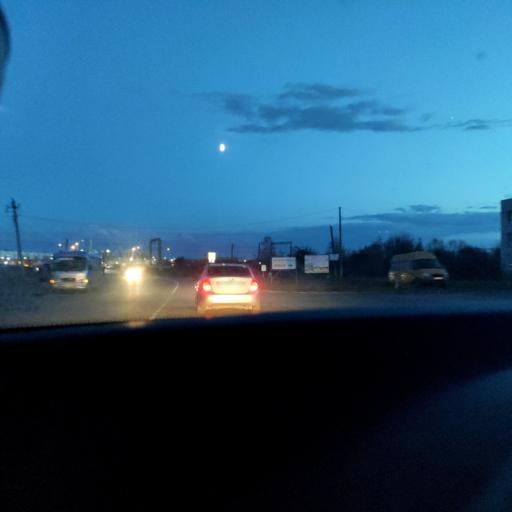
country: RU
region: Samara
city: Petra-Dubrava
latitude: 53.3097
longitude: 50.3098
